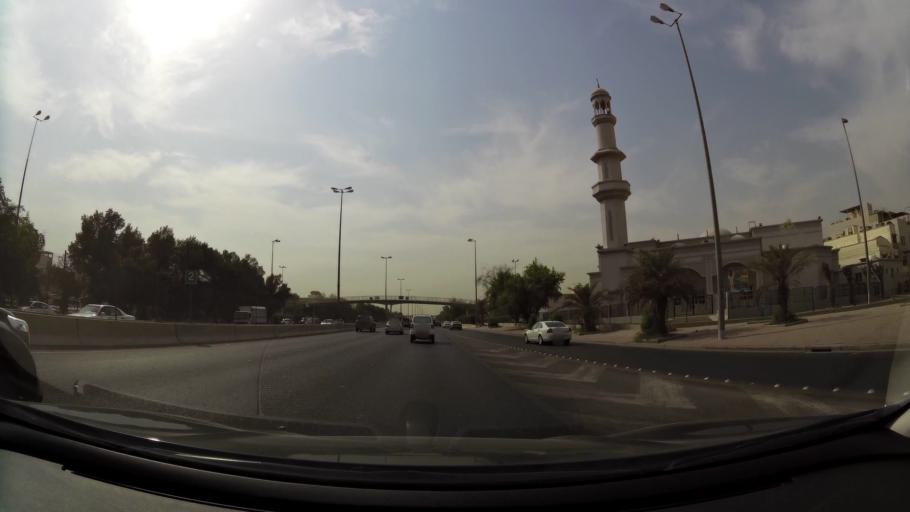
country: KW
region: Al Asimah
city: Ash Shamiyah
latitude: 29.3404
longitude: 47.9721
